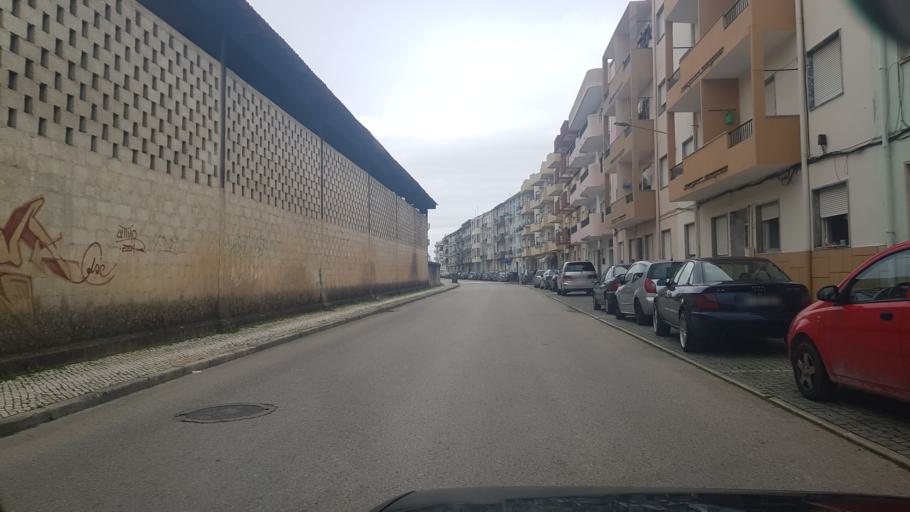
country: PT
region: Santarem
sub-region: Entroncamento
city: Entroncamento
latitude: 39.4574
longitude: -8.4757
